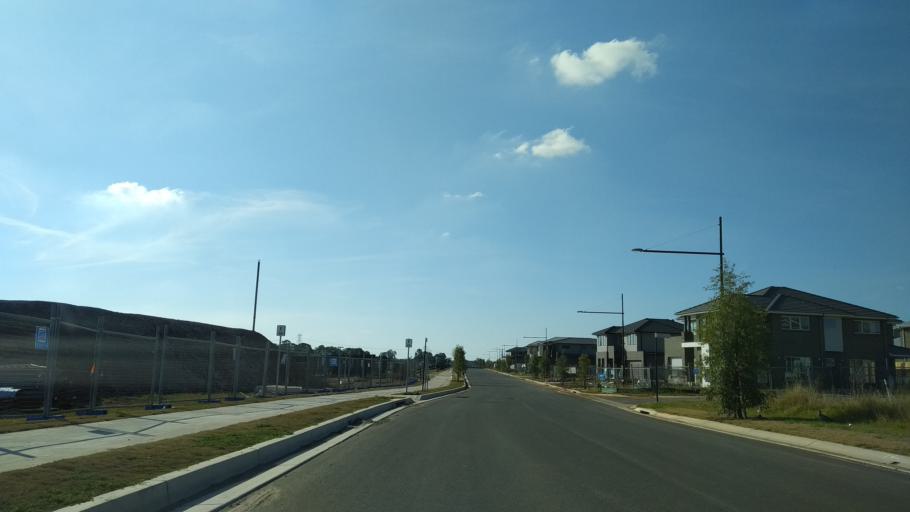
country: AU
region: New South Wales
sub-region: Blacktown
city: Blackett
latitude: -33.6922
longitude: 150.8061
